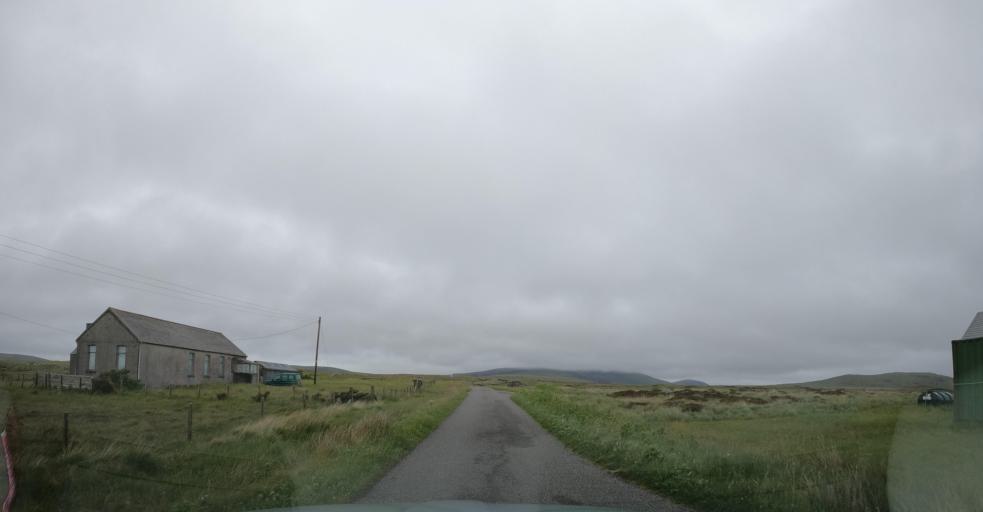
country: GB
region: Scotland
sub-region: Eilean Siar
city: Isle of North Uist
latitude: 57.5805
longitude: -7.4062
